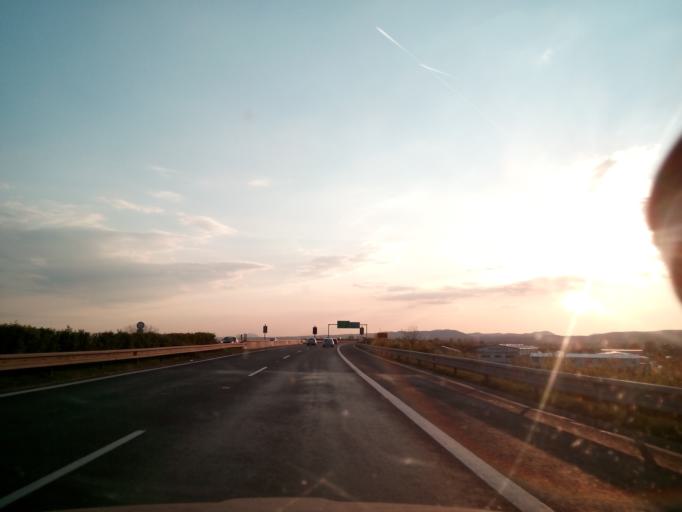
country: SK
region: Trnavsky
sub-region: Okres Trnava
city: Piestany
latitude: 48.6501
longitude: 17.8495
